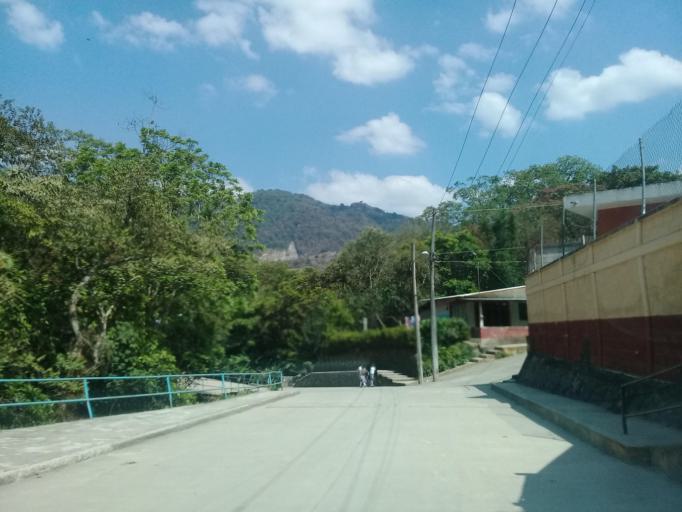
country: MX
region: Veracruz
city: Jalapilla
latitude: 18.8053
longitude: -97.0754
